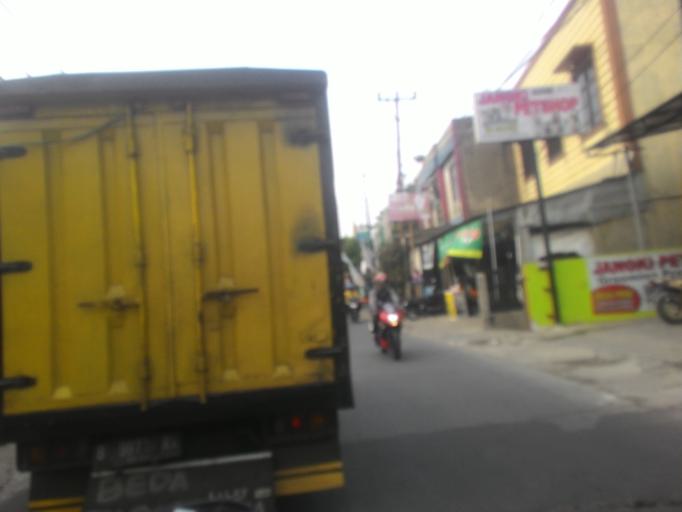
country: ID
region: West Java
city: Depok
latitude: -6.3789
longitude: 106.8136
